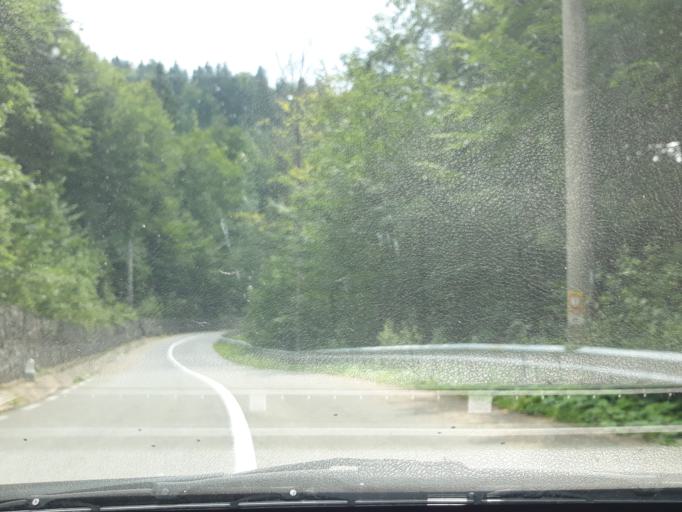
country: RO
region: Bihor
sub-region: Comuna Pietroasa
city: Pietroasa
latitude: 46.5899
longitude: 22.6749
